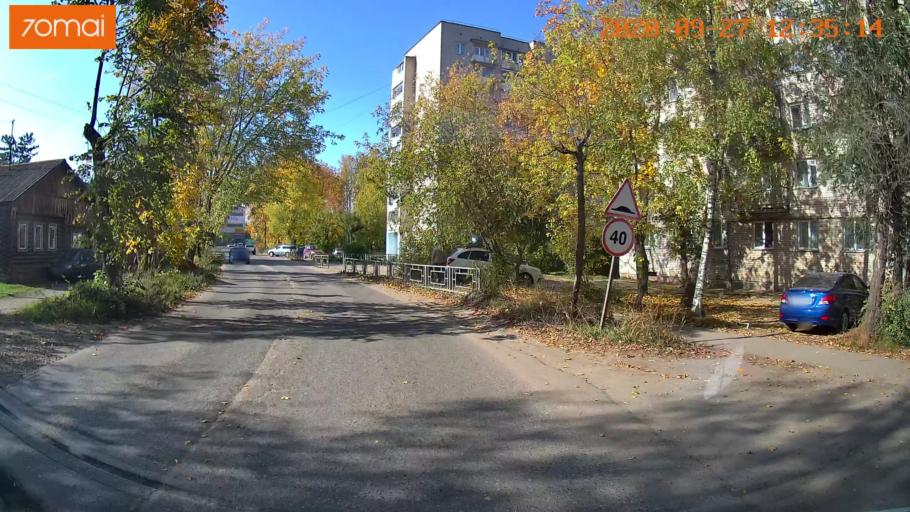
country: RU
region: Ivanovo
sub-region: Gorod Ivanovo
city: Ivanovo
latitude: 57.0188
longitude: 40.9721
